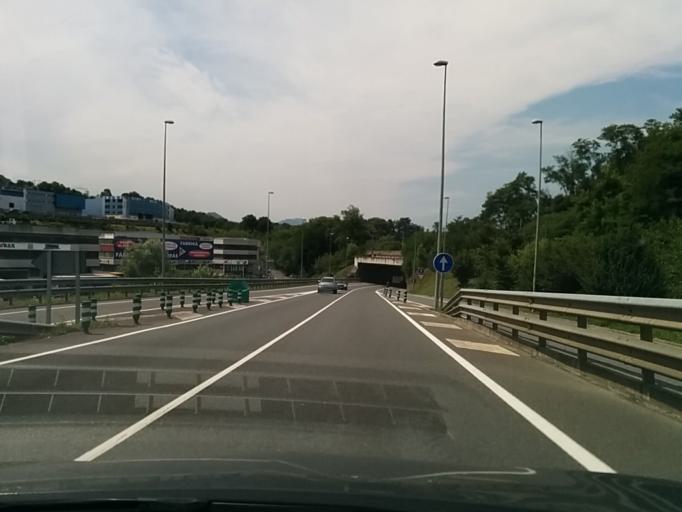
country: ES
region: Basque Country
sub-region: Provincia de Guipuzcoa
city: Lezo
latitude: 43.3197
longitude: -1.8681
